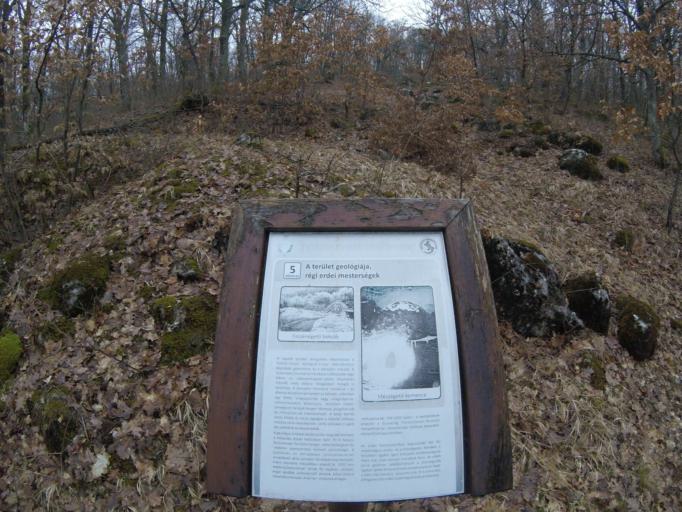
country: HU
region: Borsod-Abauj-Zemplen
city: Rudabanya
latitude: 48.4489
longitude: 20.6008
